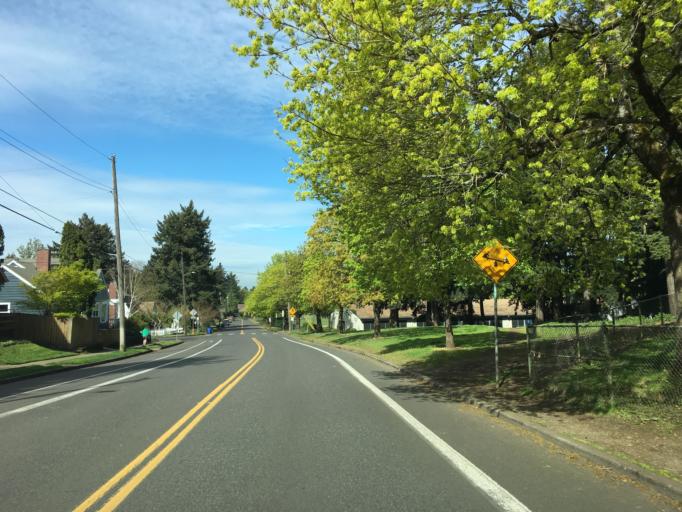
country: US
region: Oregon
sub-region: Multnomah County
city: Lents
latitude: 45.5373
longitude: -122.5953
